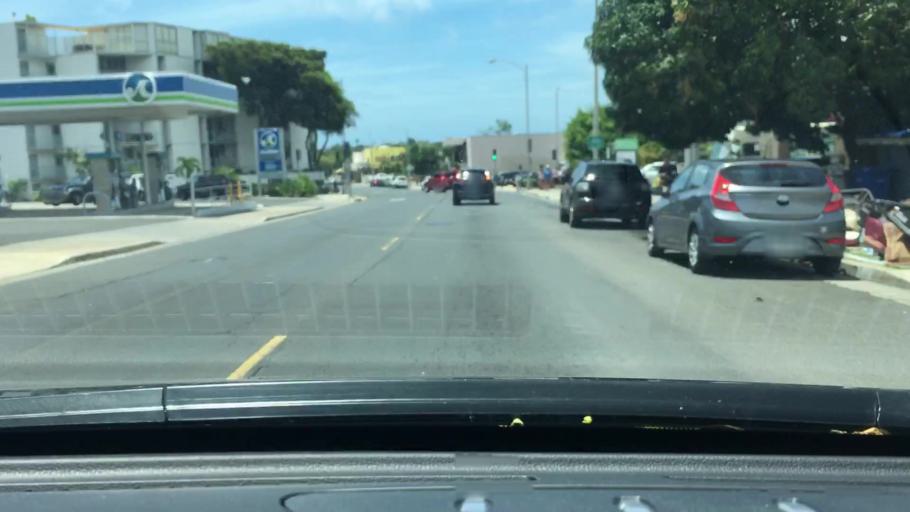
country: US
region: Hawaii
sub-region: Honolulu County
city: Honolulu
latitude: 21.2697
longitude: -157.8106
